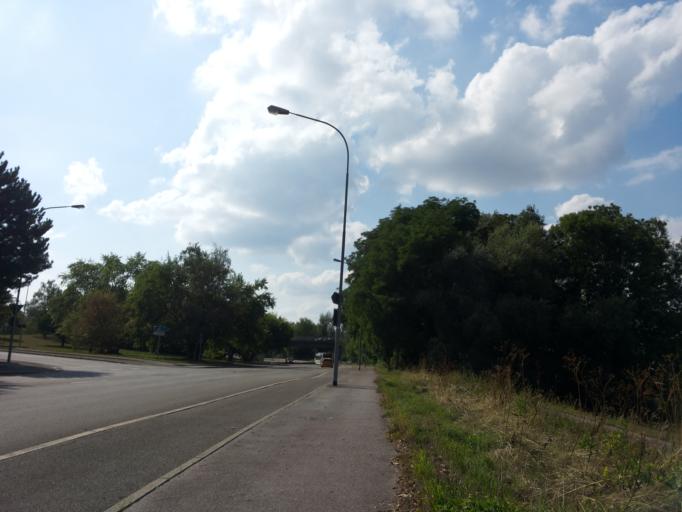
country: DE
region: Bavaria
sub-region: Upper Bavaria
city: Ingolstadt
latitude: 48.7634
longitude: 11.4423
